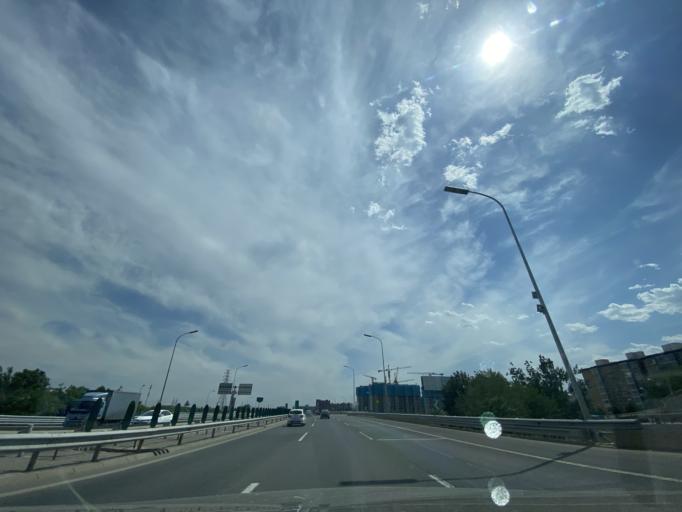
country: CN
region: Beijing
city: Lugu
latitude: 39.9420
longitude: 116.2059
